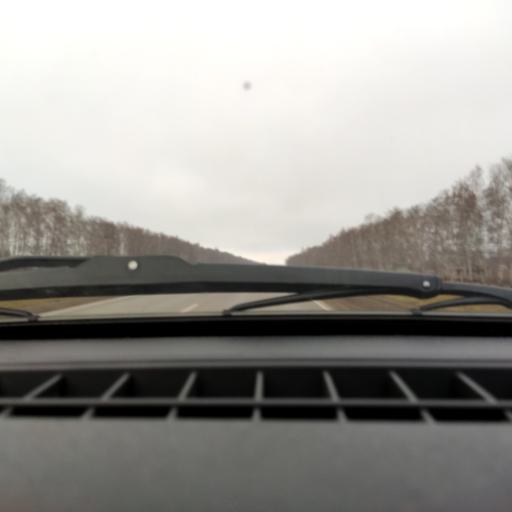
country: RU
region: Bashkortostan
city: Chishmy
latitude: 54.6156
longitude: 55.3791
